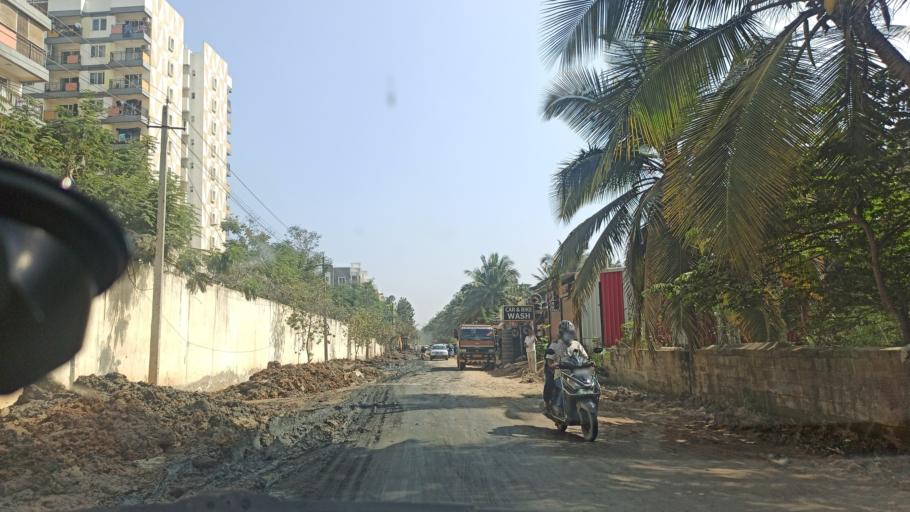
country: IN
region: Karnataka
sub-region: Bangalore Urban
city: Bangalore
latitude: 12.9154
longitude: 77.6895
